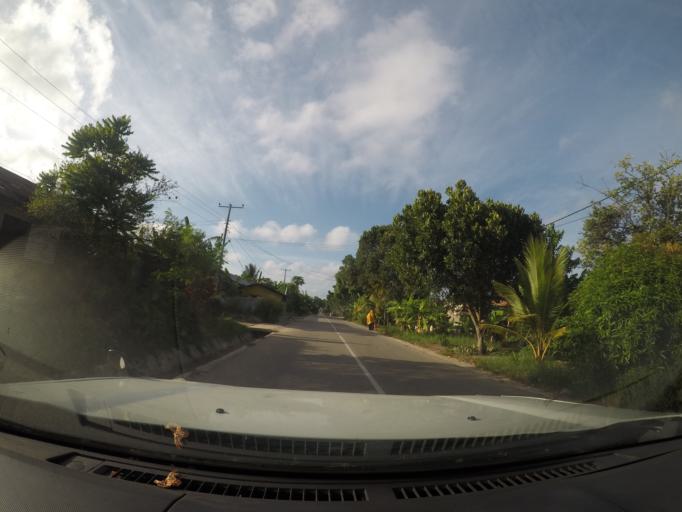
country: TZ
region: Pemba South
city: Chake Chake
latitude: -5.2451
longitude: 39.7825
